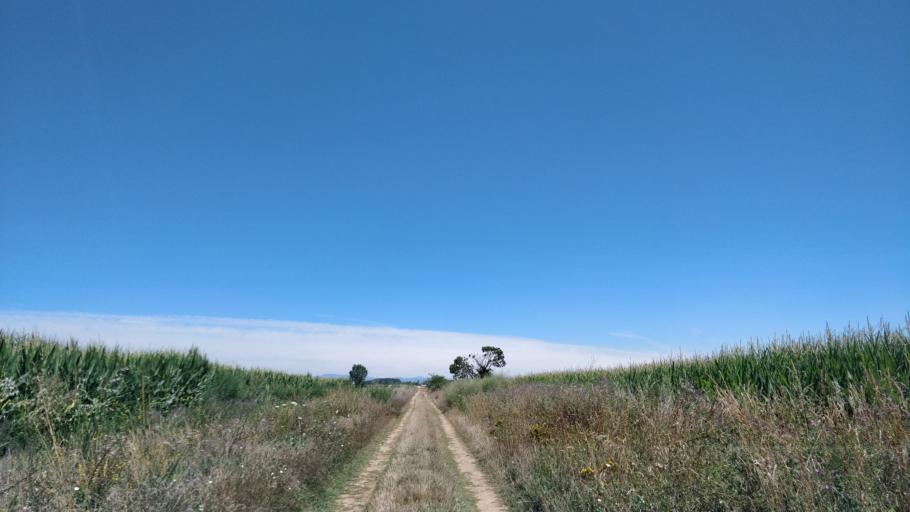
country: ES
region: Castille and Leon
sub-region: Provincia de Leon
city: Bustillo del Paramo
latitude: 42.4617
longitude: -5.8160
